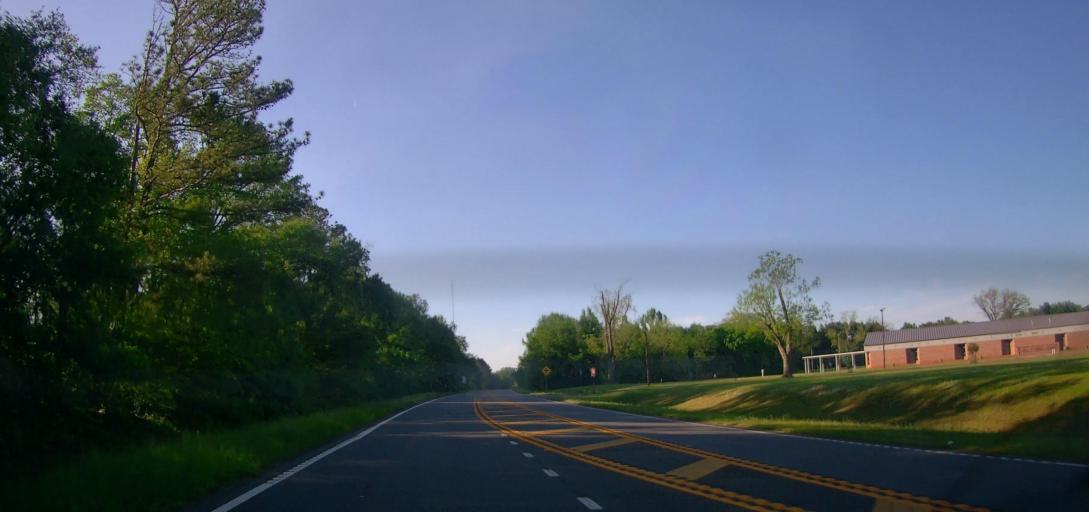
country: US
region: Georgia
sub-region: Macon County
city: Oglethorpe
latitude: 32.2880
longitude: -84.0751
